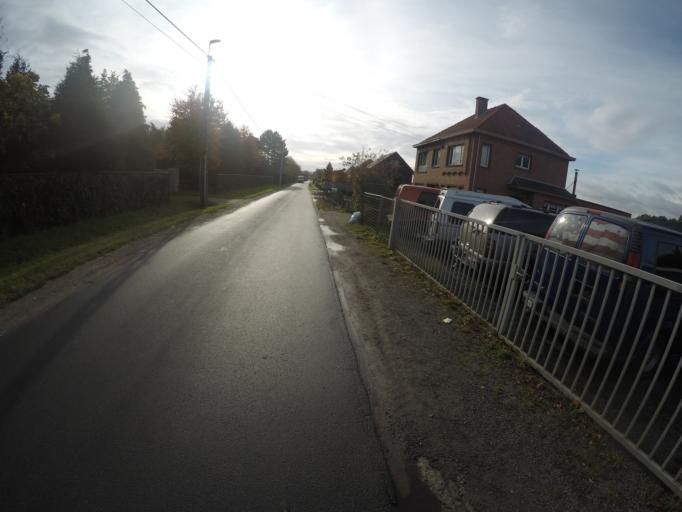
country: BE
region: Flanders
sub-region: Provincie Oost-Vlaanderen
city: Temse
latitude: 51.1569
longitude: 4.1917
